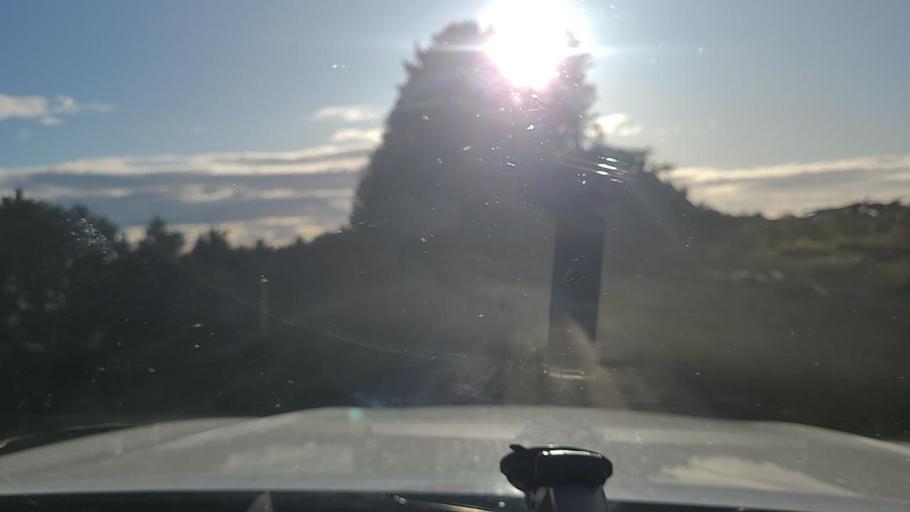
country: NZ
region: Gisborne
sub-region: Gisborne District
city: Gisborne
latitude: -38.9469
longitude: 177.8901
